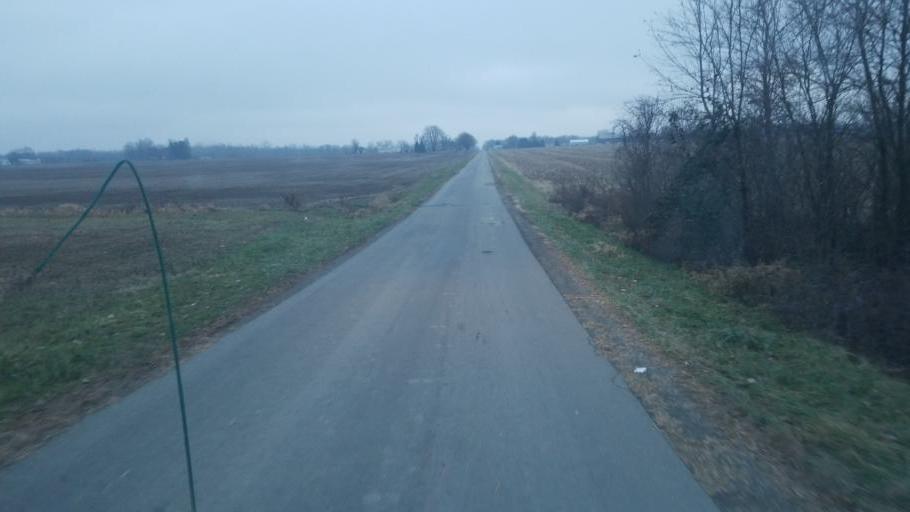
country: US
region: Ohio
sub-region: Seneca County
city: Tiffin
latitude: 40.9571
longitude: -83.1317
